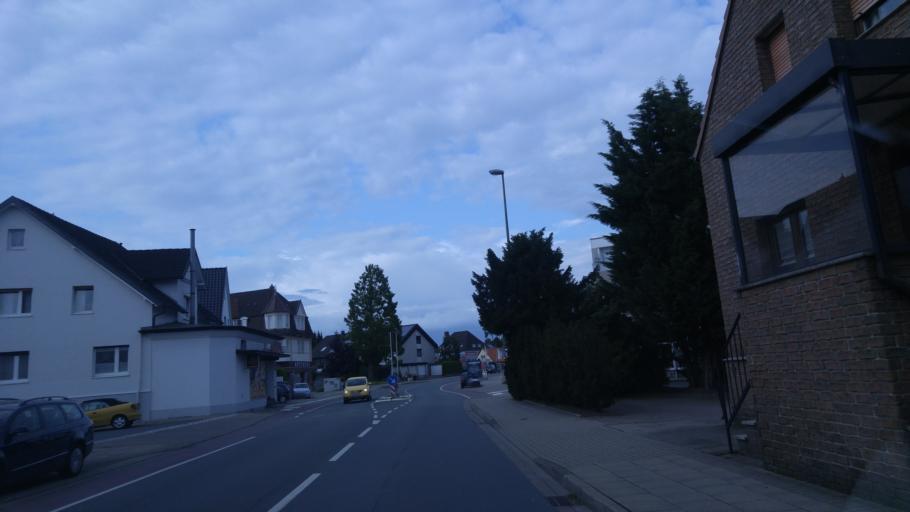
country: DE
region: North Rhine-Westphalia
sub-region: Regierungsbezirk Detmold
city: Bielefeld
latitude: 52.0488
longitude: 8.5494
